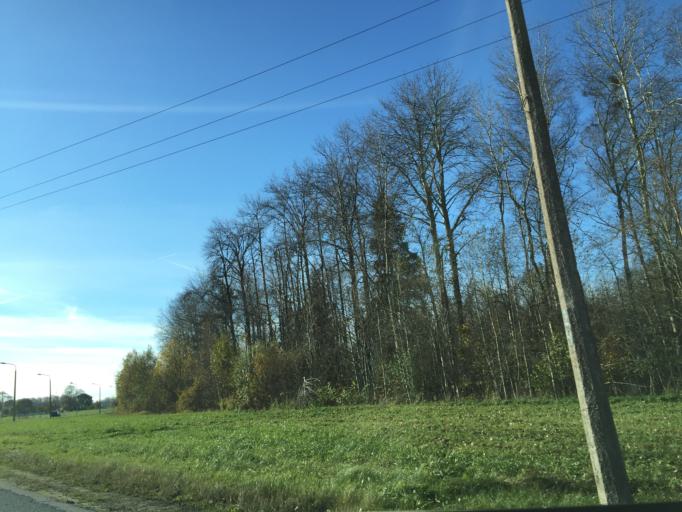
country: LV
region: Aizkraukles Rajons
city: Aizkraukle
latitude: 56.6126
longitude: 25.2696
